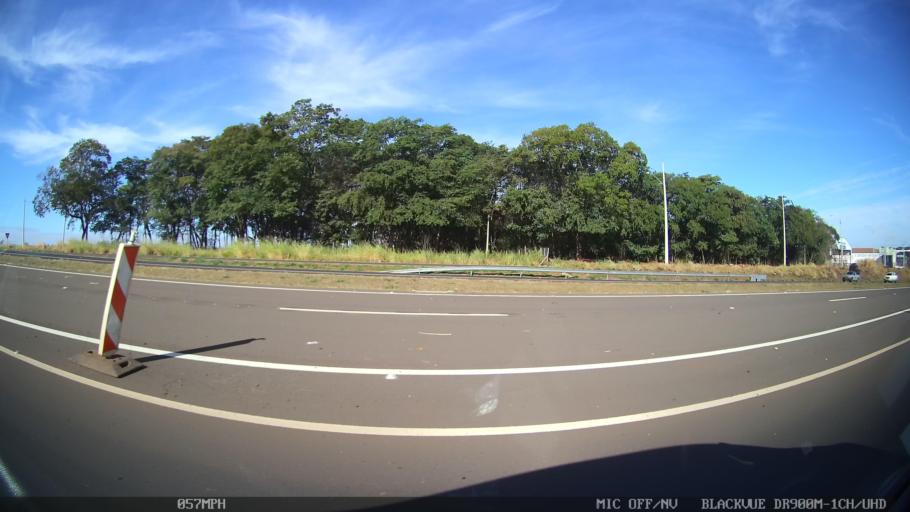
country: BR
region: Sao Paulo
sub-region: Sao Jose Do Rio Preto
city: Sao Jose do Rio Preto
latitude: -20.7690
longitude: -49.3495
